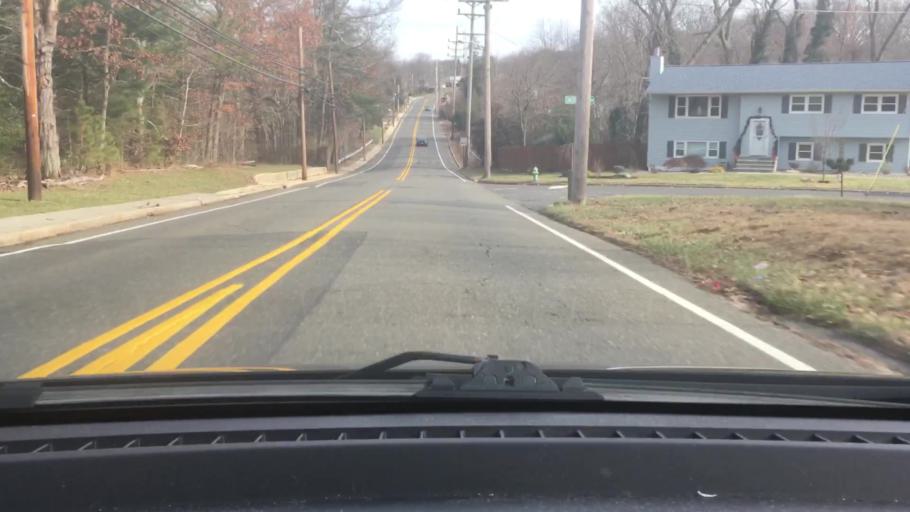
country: US
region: New Jersey
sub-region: Monmouth County
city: Shark River Hills
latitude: 40.2141
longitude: -74.0757
